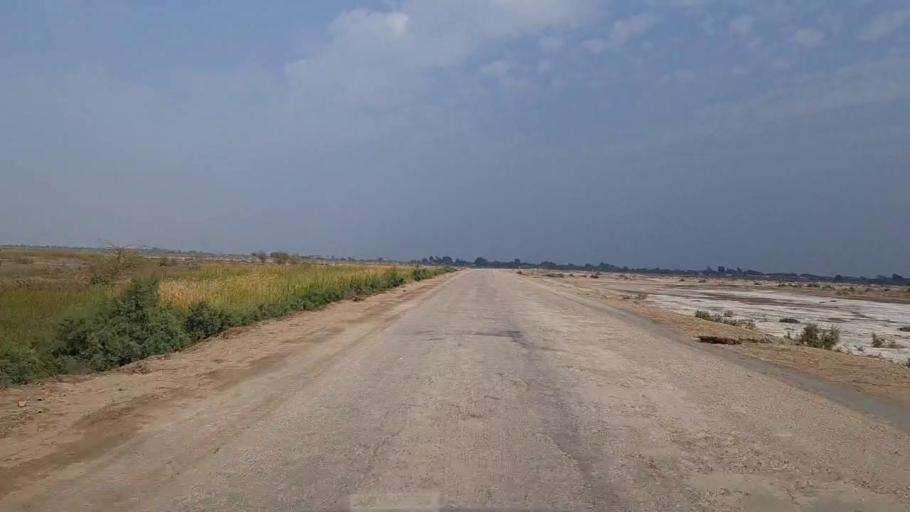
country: PK
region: Sindh
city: Mirwah Gorchani
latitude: 25.4044
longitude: 69.0569
